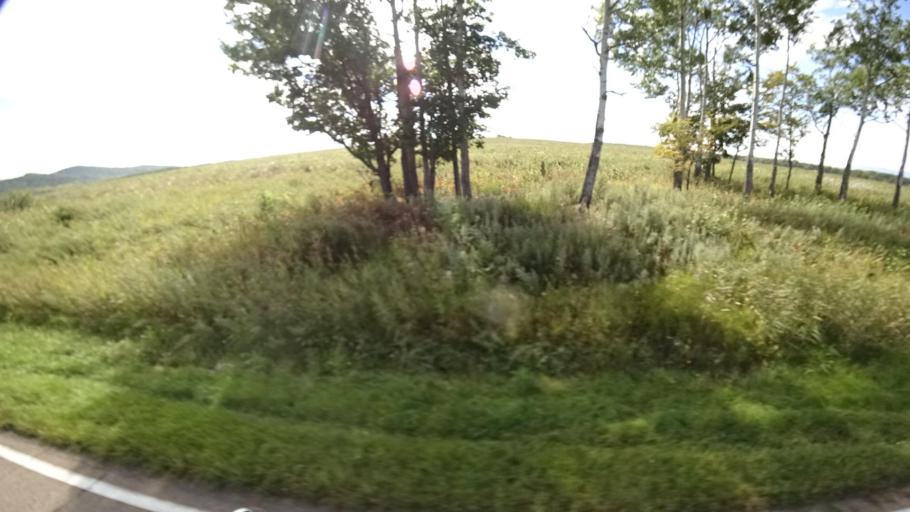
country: RU
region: Primorskiy
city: Yakovlevka
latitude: 44.4156
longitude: 133.5839
